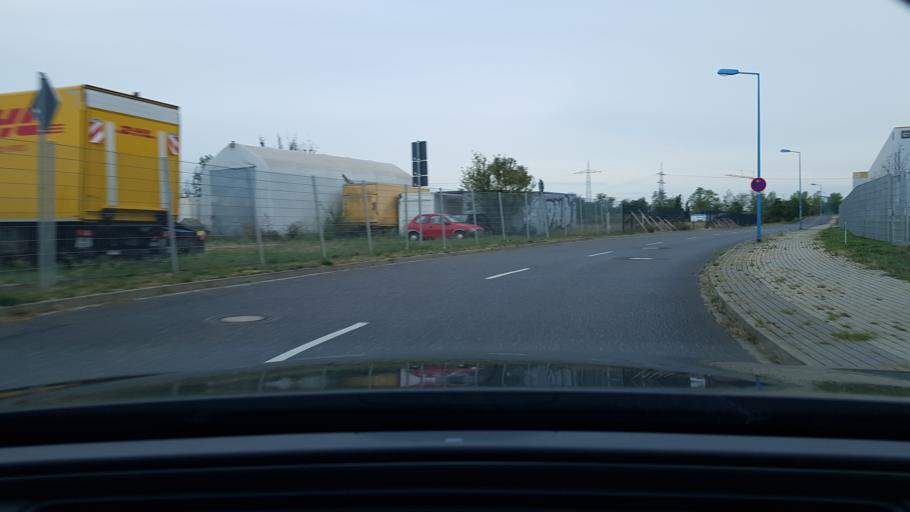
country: DE
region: Brandenburg
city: Wustermark
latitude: 52.5533
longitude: 12.9739
